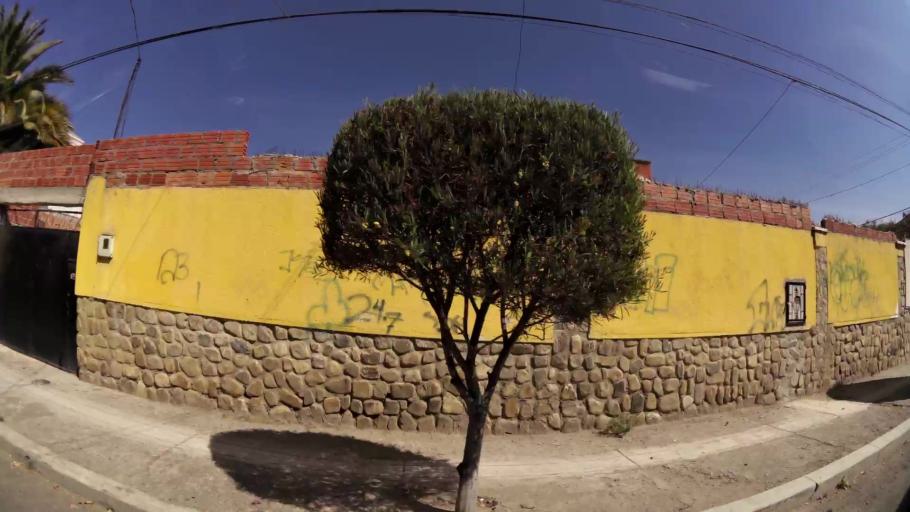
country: BO
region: La Paz
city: La Paz
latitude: -16.5282
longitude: -68.0843
